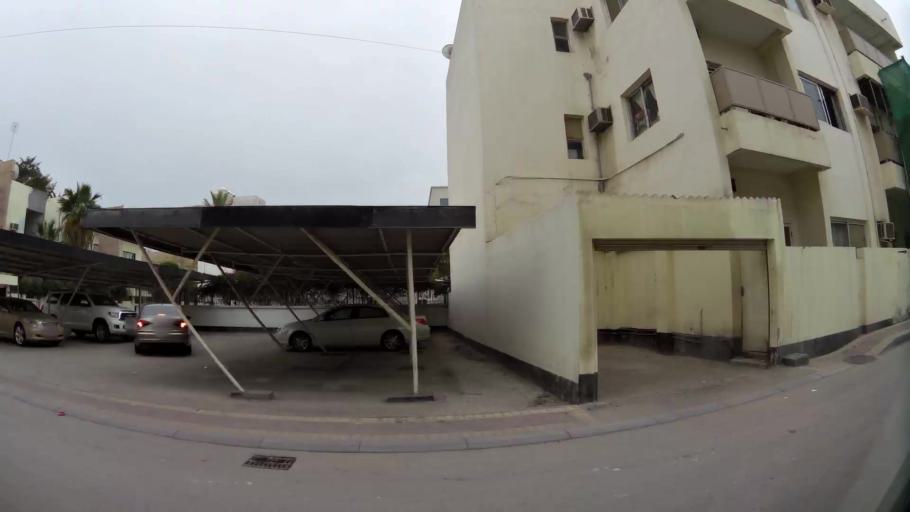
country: BH
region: Manama
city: Jidd Hafs
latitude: 26.2225
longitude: 50.5660
